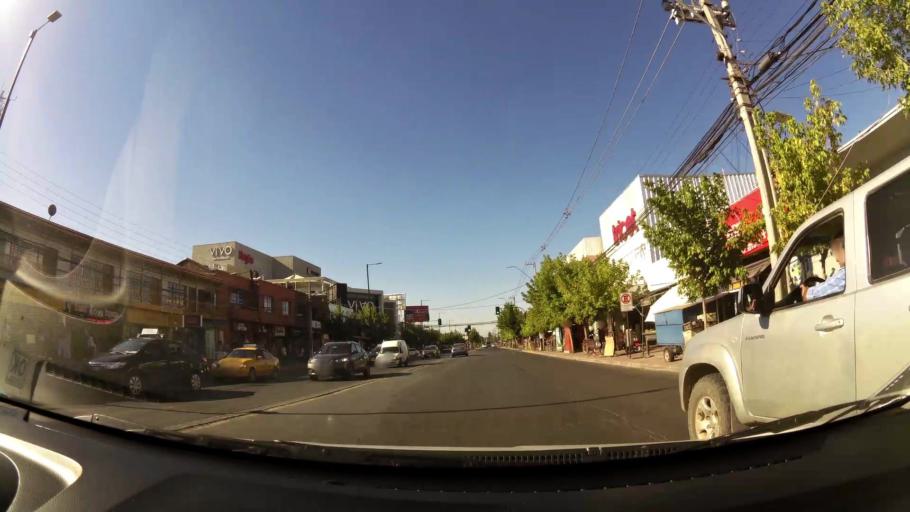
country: CL
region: O'Higgins
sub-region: Provincia de Colchagua
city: Chimbarongo
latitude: -34.5874
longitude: -70.9850
